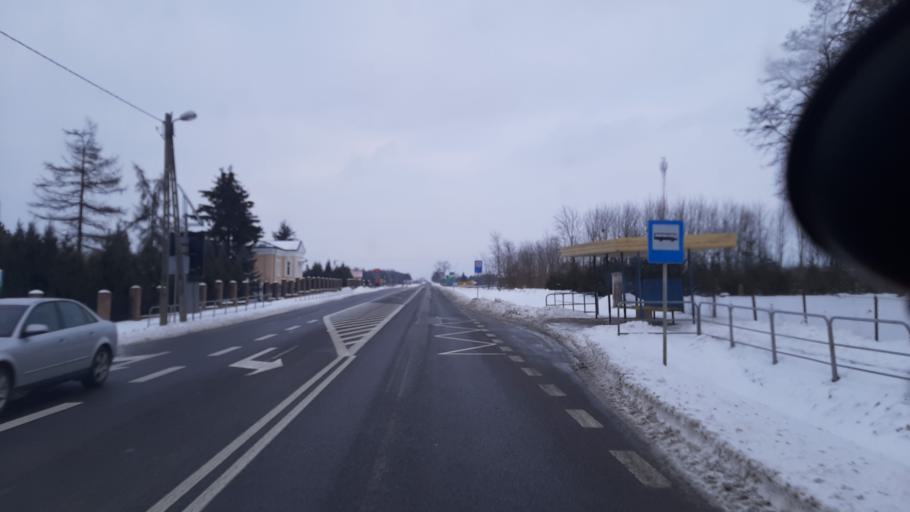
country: PL
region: Lublin Voivodeship
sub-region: Powiat pulawski
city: Kurow
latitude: 51.3870
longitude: 22.2029
